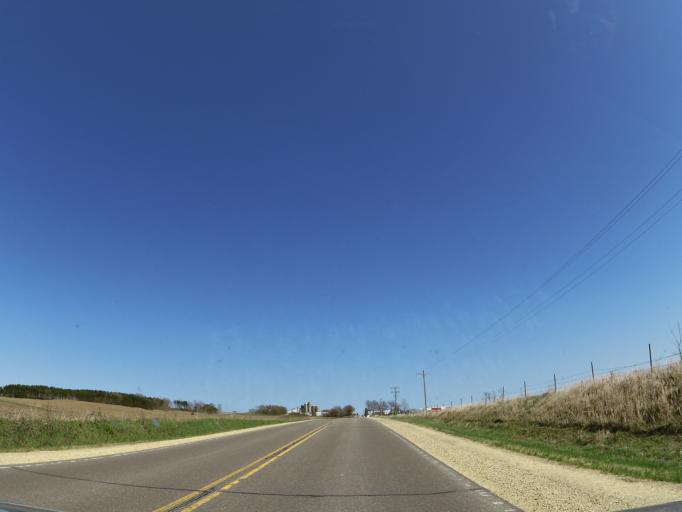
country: US
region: Wisconsin
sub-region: Saint Croix County
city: Hammond
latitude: 44.9347
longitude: -92.4828
